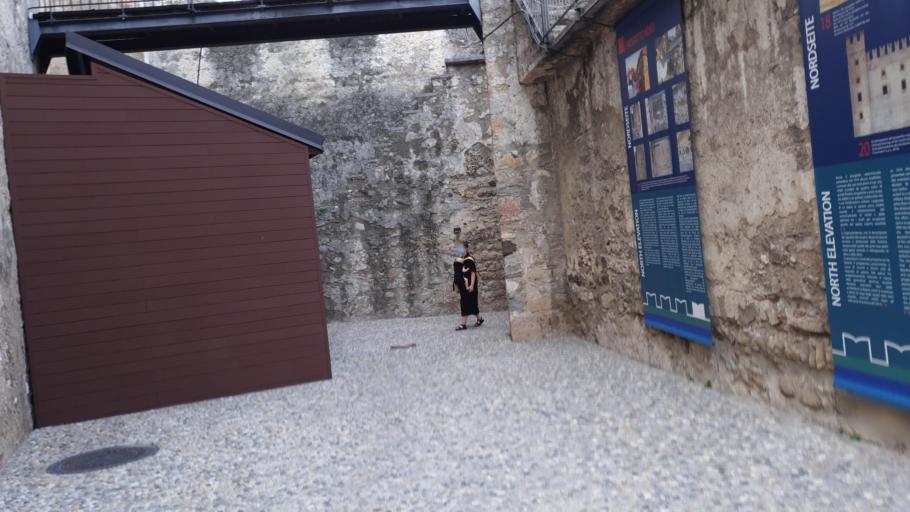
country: IT
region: Lombardy
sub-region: Provincia di Brescia
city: Sirmione
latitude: 45.4923
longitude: 10.6087
